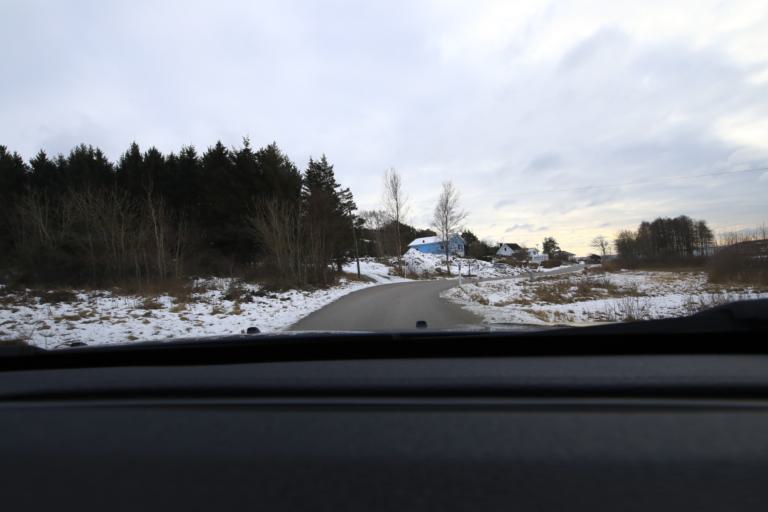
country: SE
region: Halland
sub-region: Kungsbacka Kommun
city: Frillesas
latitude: 57.2179
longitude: 12.1574
